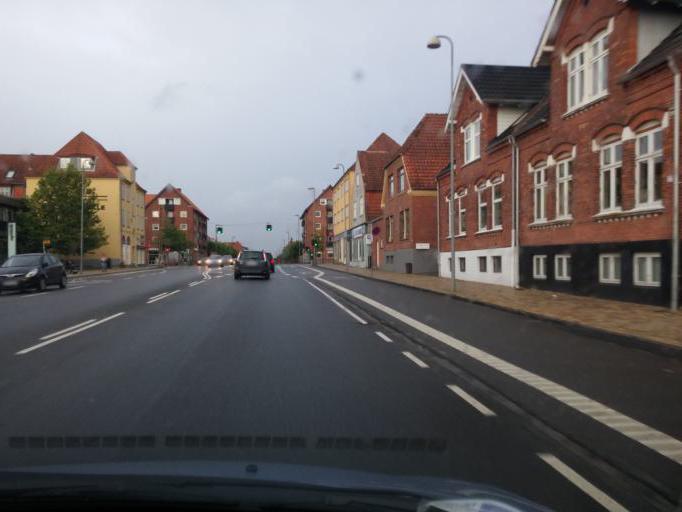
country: DK
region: South Denmark
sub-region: Odense Kommune
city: Odense
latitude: 55.3938
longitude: 10.3496
